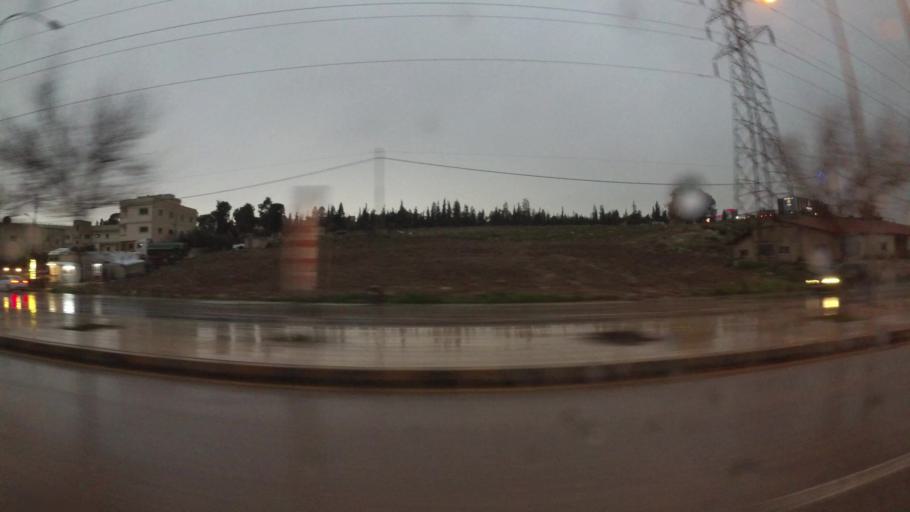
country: JO
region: Amman
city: Umm as Summaq
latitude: 31.9168
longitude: 35.8617
